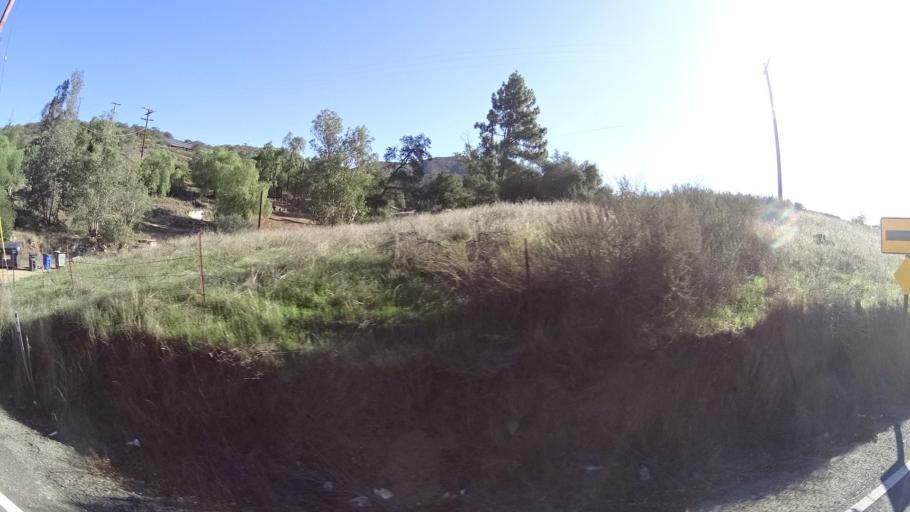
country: MX
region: Baja California
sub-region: Tijuana
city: Villa del Campo
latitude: 32.6328
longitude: -116.7639
